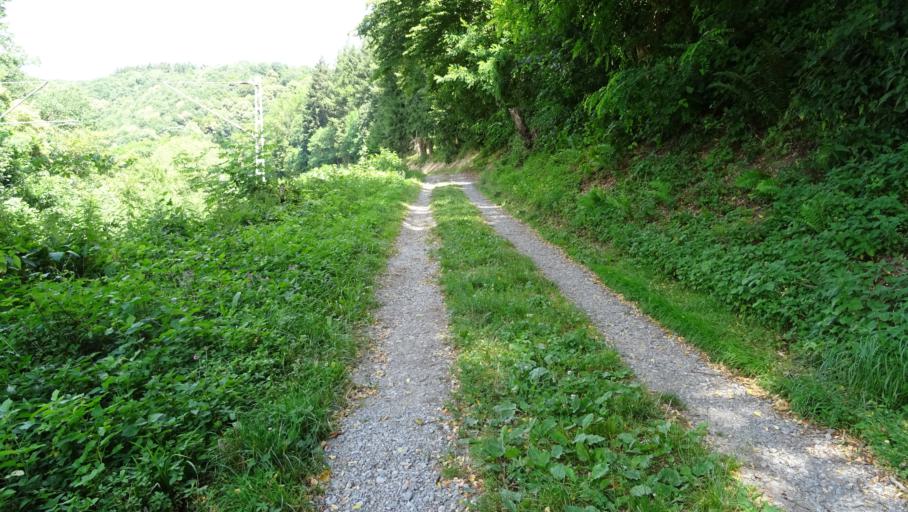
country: DE
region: Baden-Wuerttemberg
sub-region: Karlsruhe Region
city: Neckargerach
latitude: 49.3854
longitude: 9.0842
